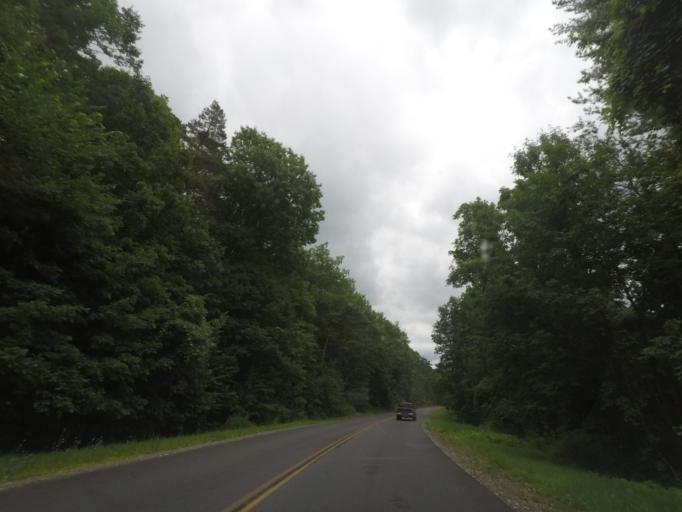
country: US
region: New York
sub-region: Rensselaer County
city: Poestenkill
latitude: 42.8241
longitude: -73.5168
